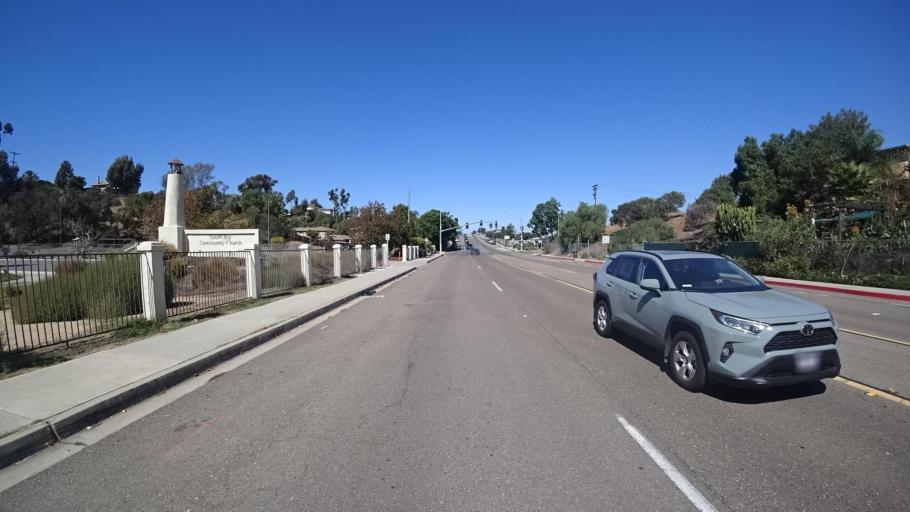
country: US
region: California
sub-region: San Diego County
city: National City
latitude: 32.6682
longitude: -117.0768
